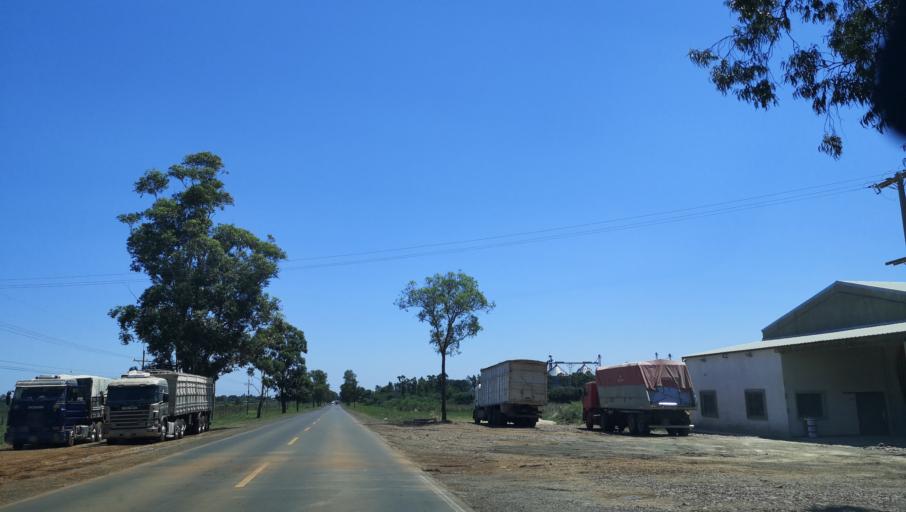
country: PY
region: Itapua
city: Carmen del Parana
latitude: -27.2212
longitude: -56.1237
